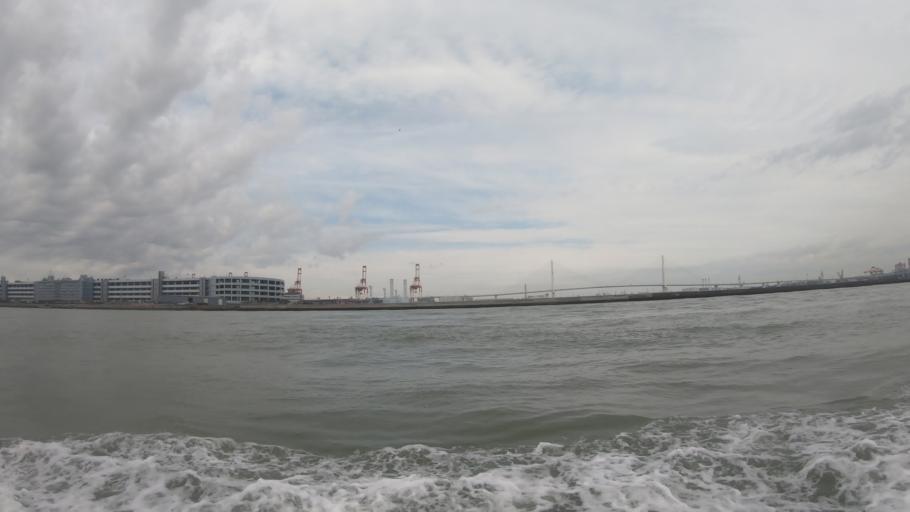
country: JP
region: Kanagawa
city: Yokohama
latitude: 35.4540
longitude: 139.7060
